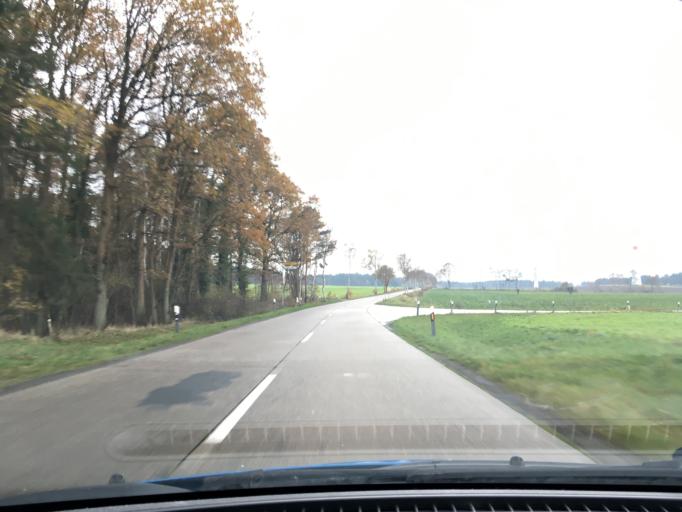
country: DE
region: Lower Saxony
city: Sudergellersen
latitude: 53.1918
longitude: 10.3134
